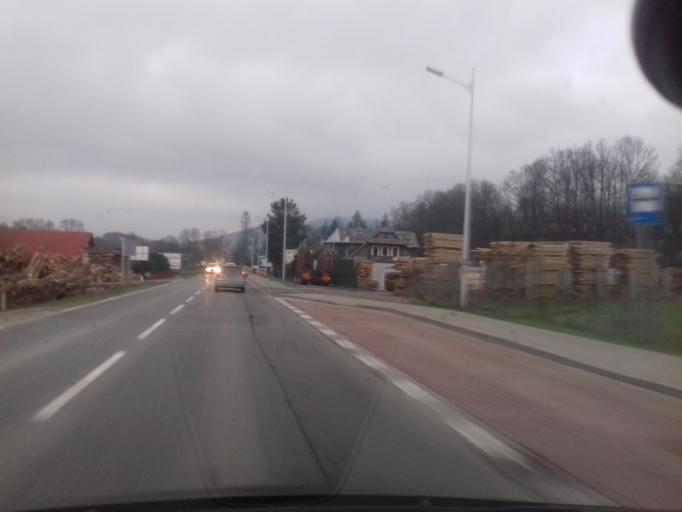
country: PL
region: Lesser Poland Voivodeship
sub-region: Powiat limanowski
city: Mszana Dolna
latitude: 49.6910
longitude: 20.0455
